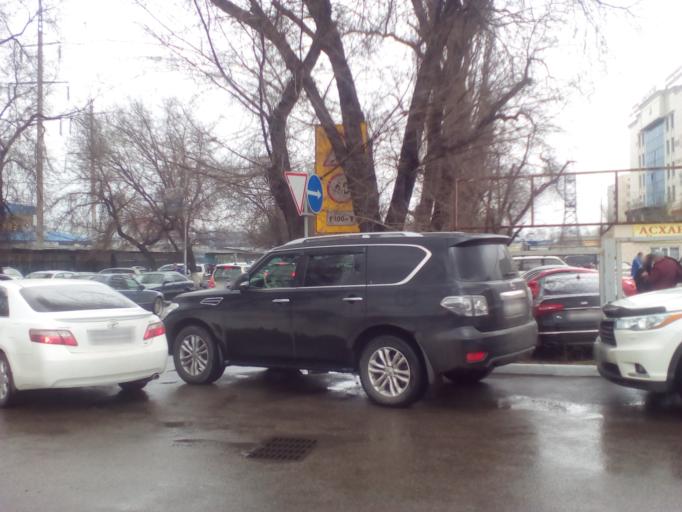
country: KZ
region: Almaty Qalasy
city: Almaty
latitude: 43.2386
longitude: 76.8238
